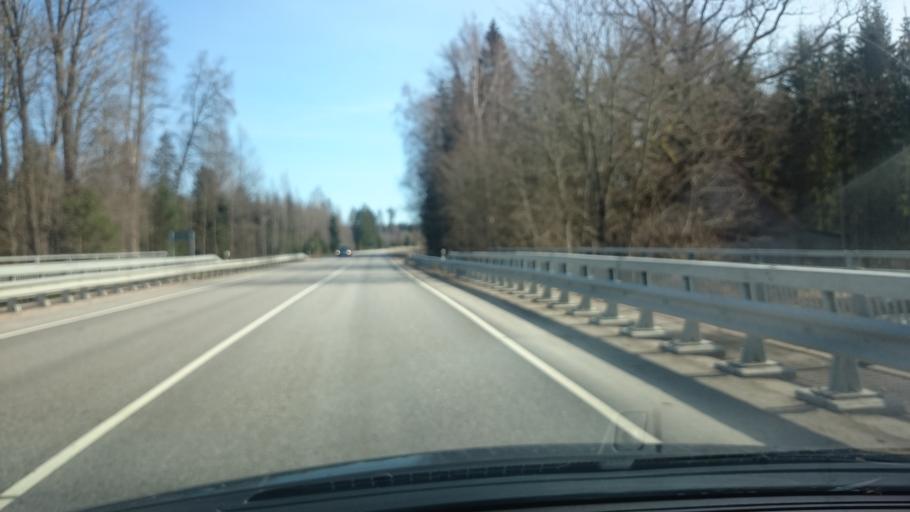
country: EE
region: Paernumaa
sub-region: Vaendra vald (alev)
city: Vandra
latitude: 58.6732
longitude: 25.1209
